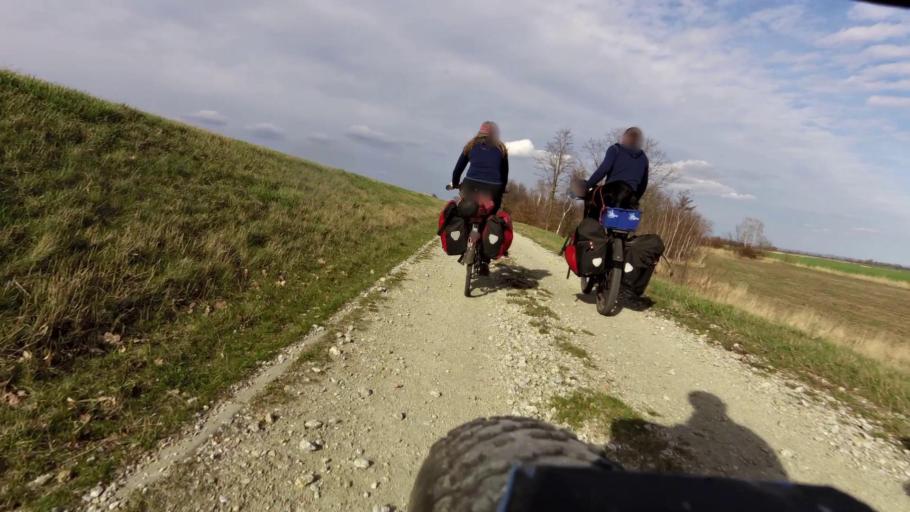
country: DE
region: Brandenburg
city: Reitwein
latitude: 52.5402
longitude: 14.6164
